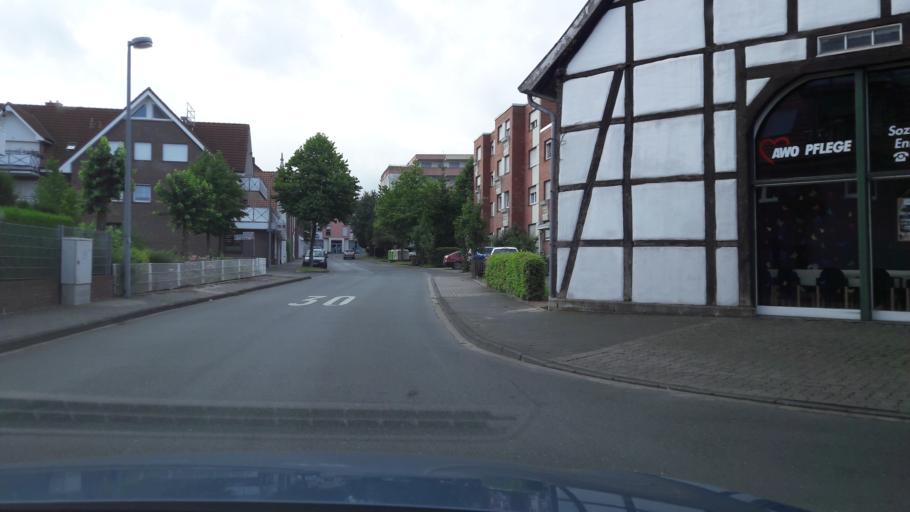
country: DE
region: North Rhine-Westphalia
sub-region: Regierungsbezirk Munster
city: Ennigerloh
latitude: 51.8374
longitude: 8.0230
